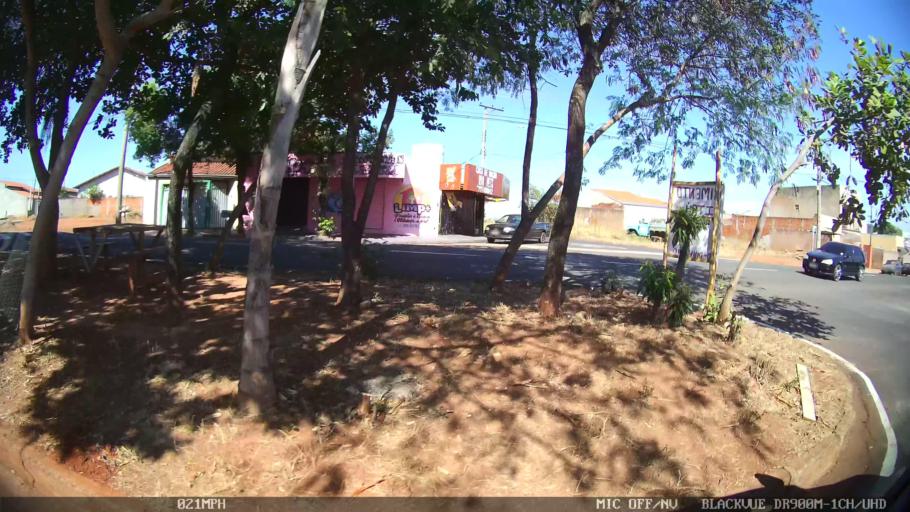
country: BR
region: Sao Paulo
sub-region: Sao Jose Do Rio Preto
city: Sao Jose do Rio Preto
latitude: -20.7655
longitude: -49.4044
